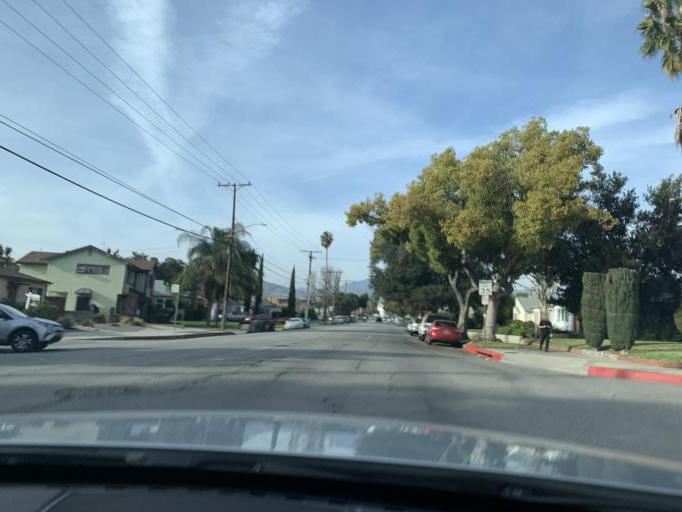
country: US
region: California
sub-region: Los Angeles County
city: Glendale
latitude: 34.1371
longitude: -118.2336
